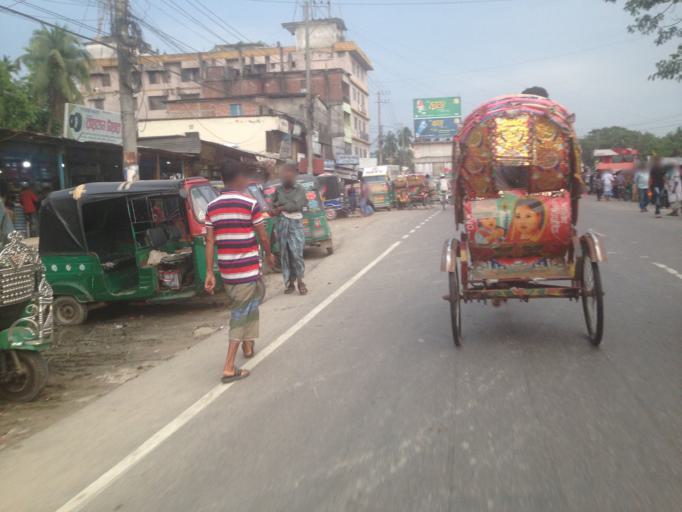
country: BD
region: Chittagong
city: Lakshmipur
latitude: 22.9449
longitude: 90.8271
